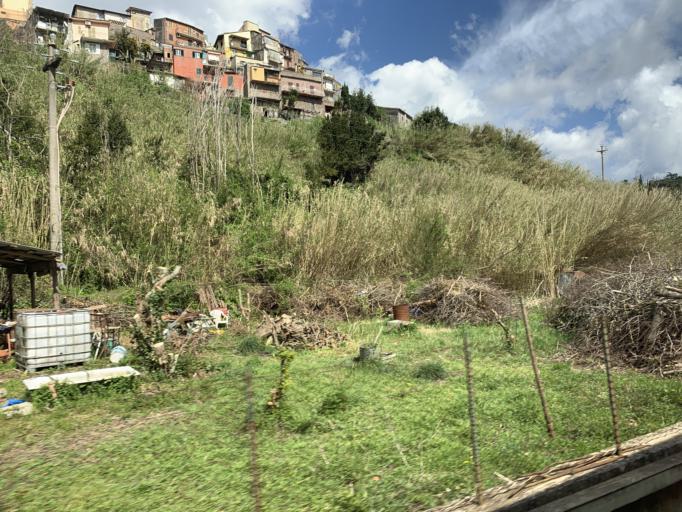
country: IT
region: Latium
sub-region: Citta metropolitana di Roma Capitale
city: Castel Gandolfo
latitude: 41.7675
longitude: 12.6599
